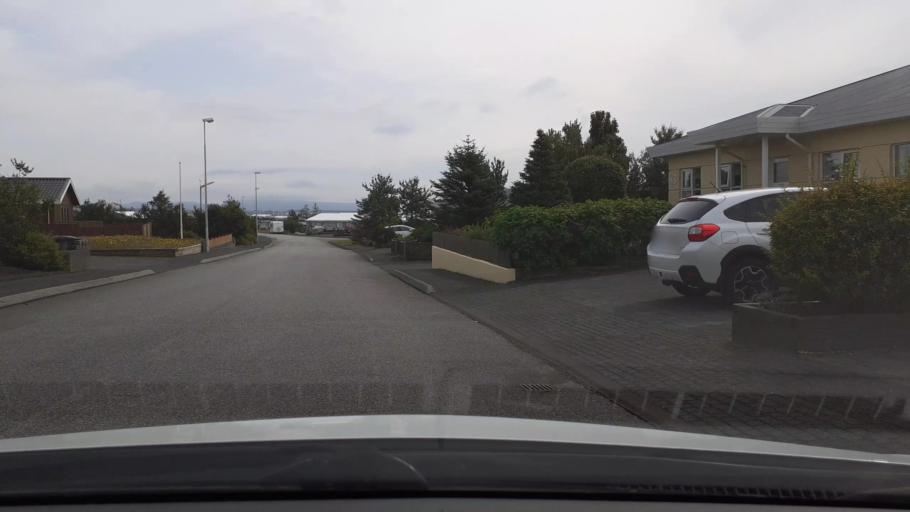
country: IS
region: Southern Peninsula
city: Reykjanesbaer
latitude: 63.9972
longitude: -22.5739
